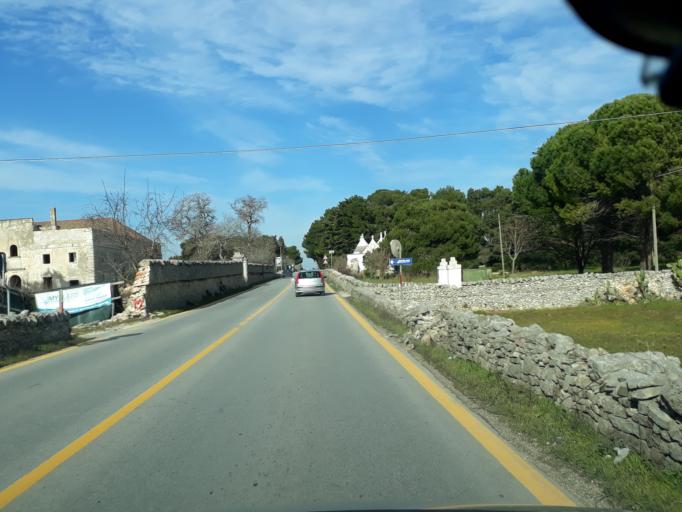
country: IT
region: Apulia
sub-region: Provincia di Taranto
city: Martina Franca
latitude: 40.7200
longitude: 17.3327
